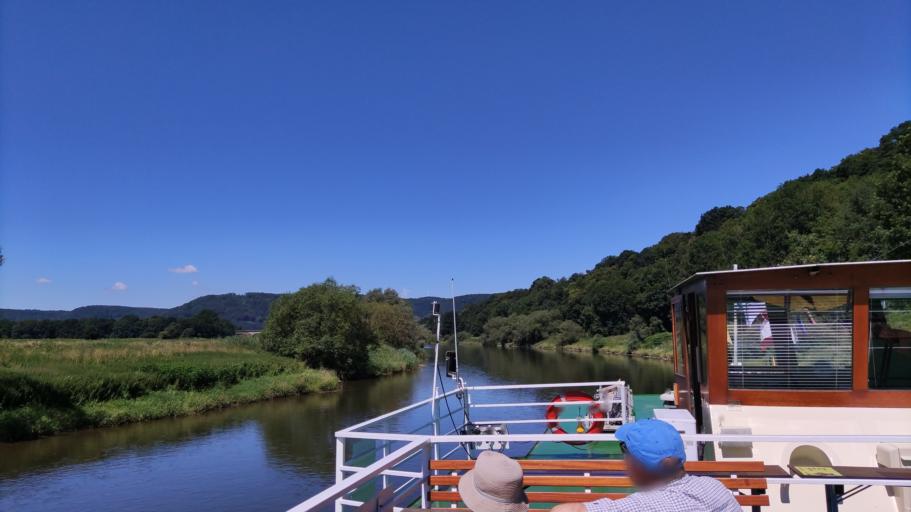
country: DE
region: Lower Saxony
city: Furstenberg
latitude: 51.7324
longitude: 9.3939
